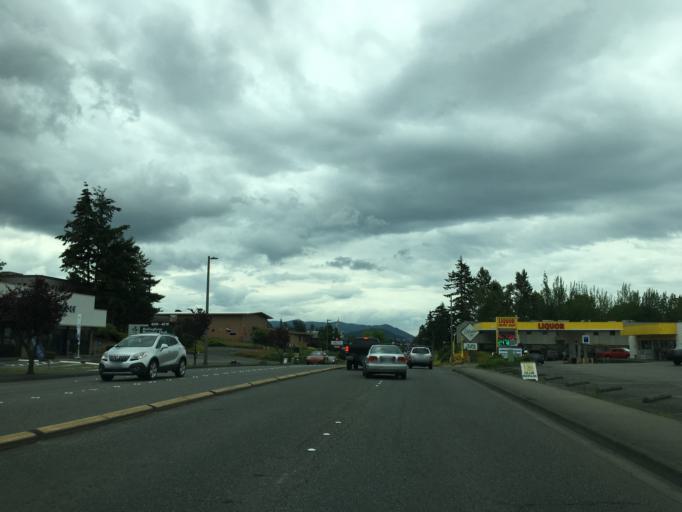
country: US
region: Washington
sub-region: Whatcom County
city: Bellingham
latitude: 48.7944
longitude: -122.4861
